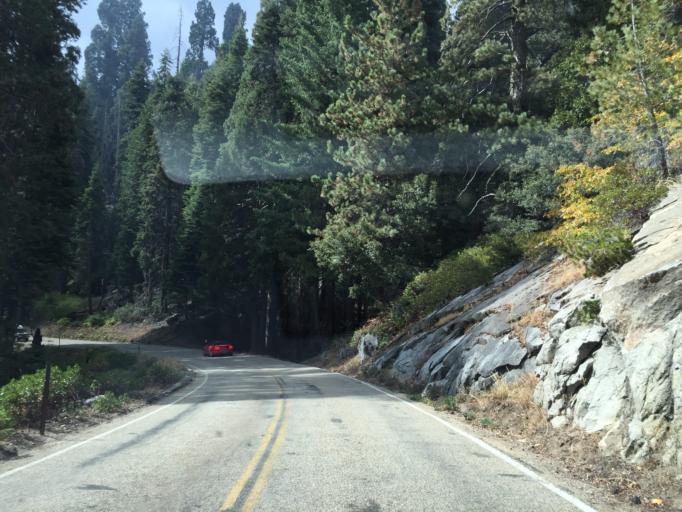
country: US
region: California
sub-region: Tulare County
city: Three Rivers
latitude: 36.7200
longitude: -118.9206
